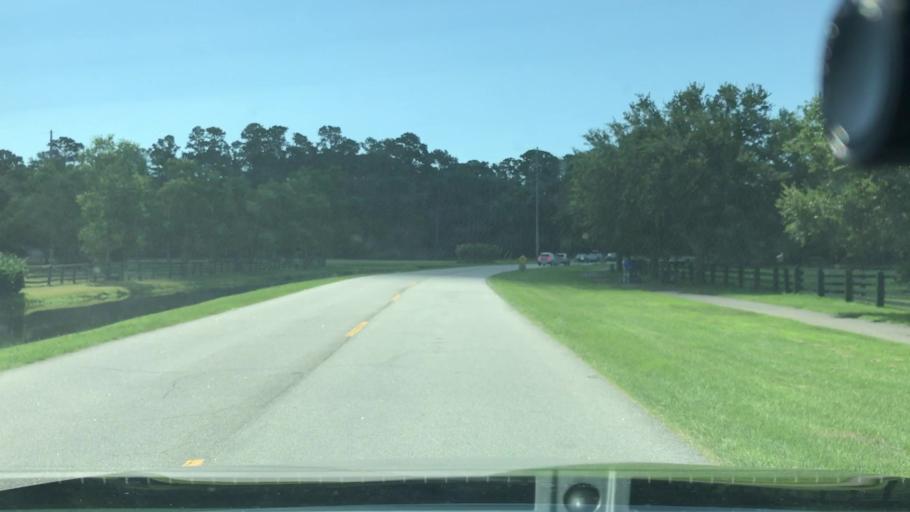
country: US
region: South Carolina
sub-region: Beaufort County
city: Hilton Head Island
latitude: 32.1413
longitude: -80.7886
